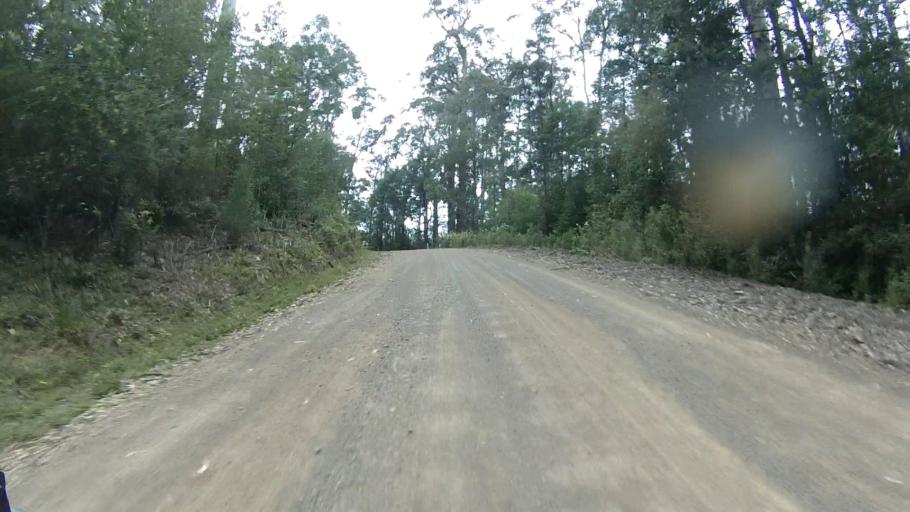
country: AU
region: Tasmania
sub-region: Sorell
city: Sorell
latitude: -42.7003
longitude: 147.8550
